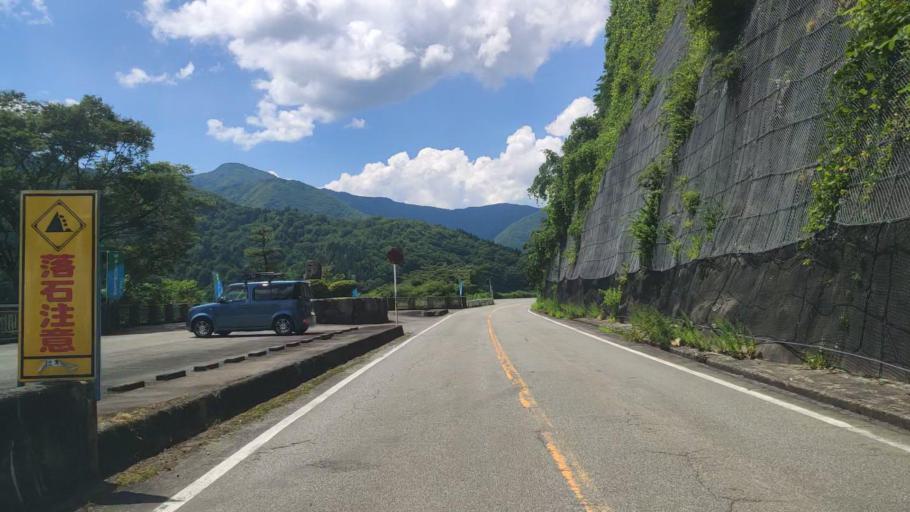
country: JP
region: Fukui
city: Ono
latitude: 35.9181
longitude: 136.5397
